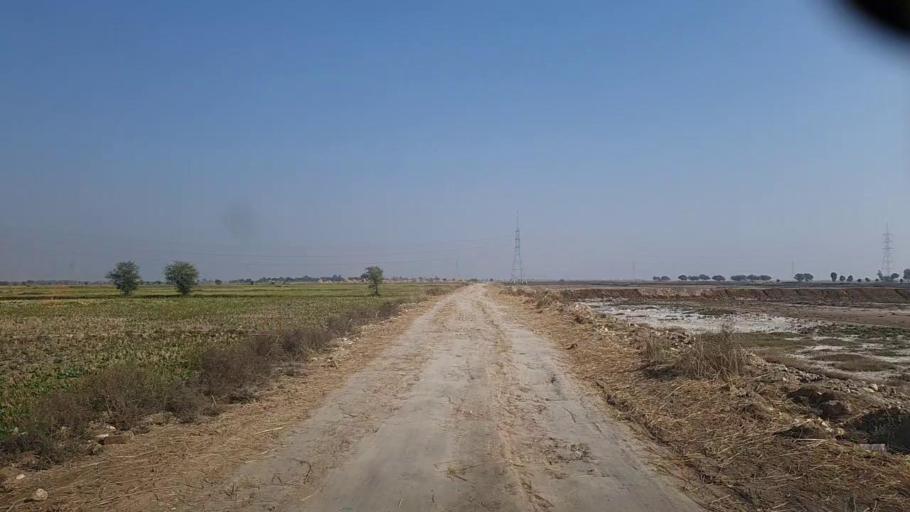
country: PK
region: Sindh
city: Jacobabad
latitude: 28.3078
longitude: 68.5911
